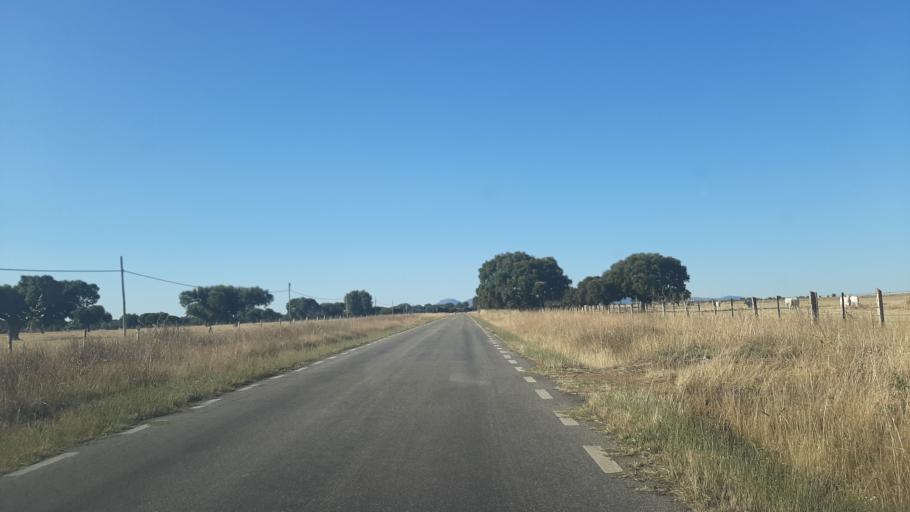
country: ES
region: Castille and Leon
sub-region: Provincia de Salamanca
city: Cabrillas
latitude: 40.7146
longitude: -6.1786
